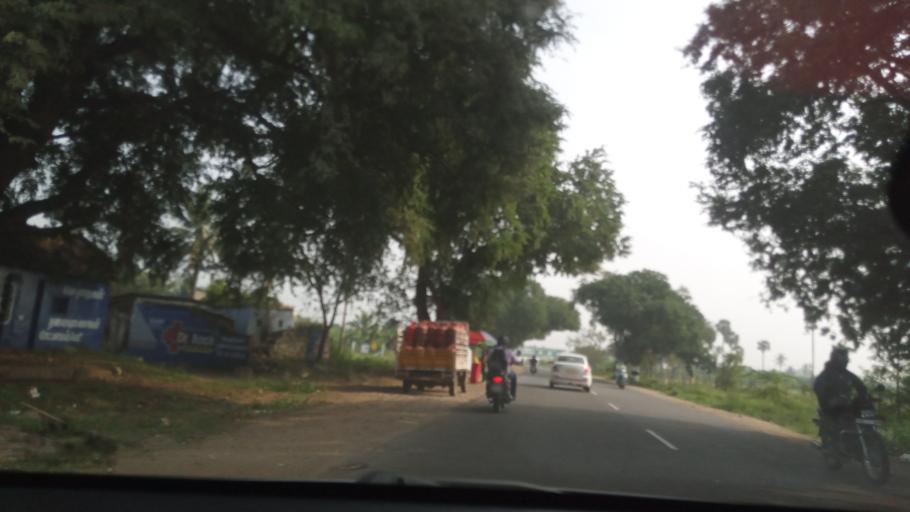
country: IN
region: Tamil Nadu
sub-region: Coimbatore
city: Periyanayakkanpalaiyam
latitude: 11.1464
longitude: 77.0432
